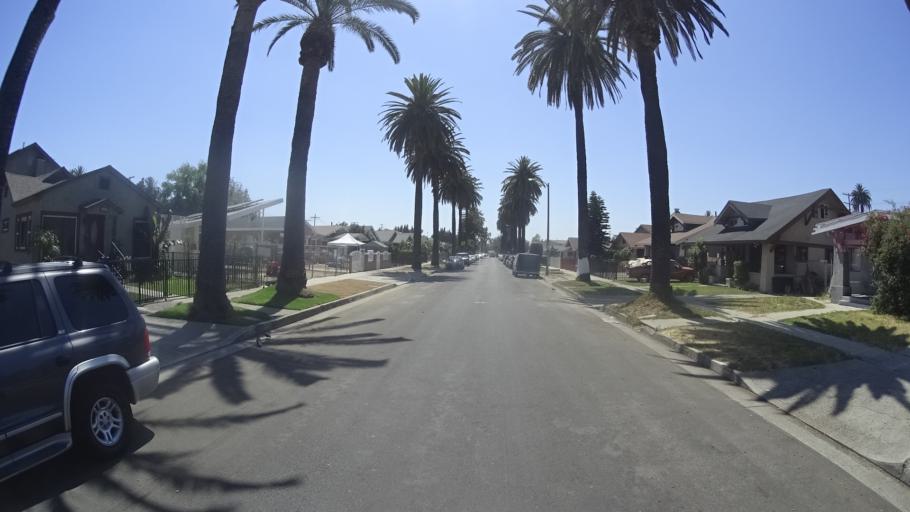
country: US
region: California
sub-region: Los Angeles County
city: View Park-Windsor Hills
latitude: 34.0157
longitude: -118.3113
